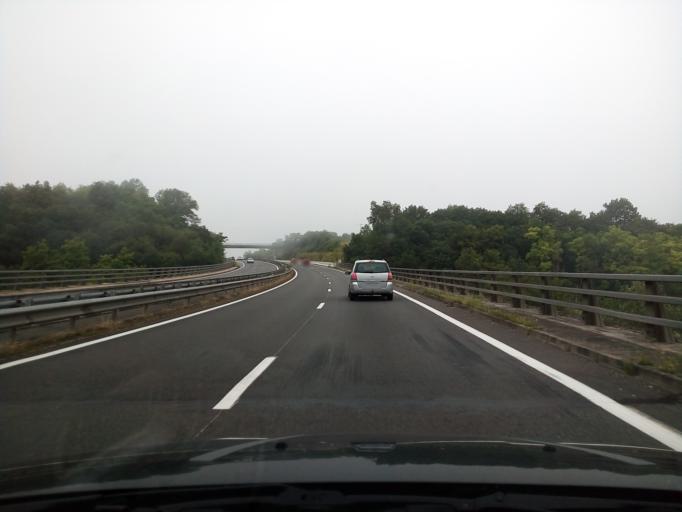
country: FR
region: Poitou-Charentes
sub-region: Departement de la Charente
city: Chassors
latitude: 45.6682
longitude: -0.2128
